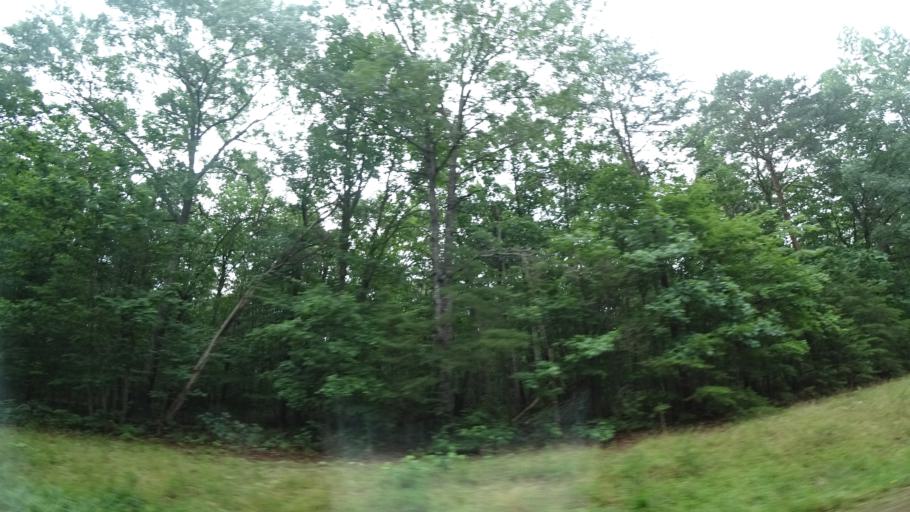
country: US
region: Virginia
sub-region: Louisa County
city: Louisa
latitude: 38.1371
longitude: -77.8178
